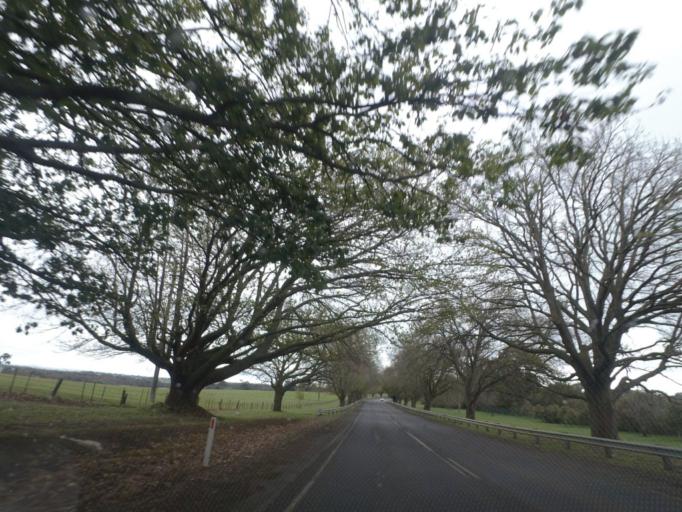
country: AU
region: Victoria
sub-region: Hume
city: Sunbury
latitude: -37.3396
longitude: 144.5272
